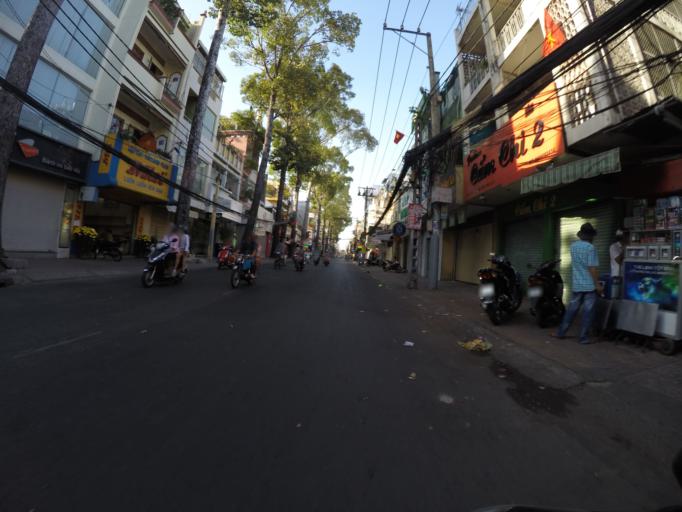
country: VN
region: Ho Chi Minh City
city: Quan Phu Nhuan
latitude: 10.7886
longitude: 106.6782
